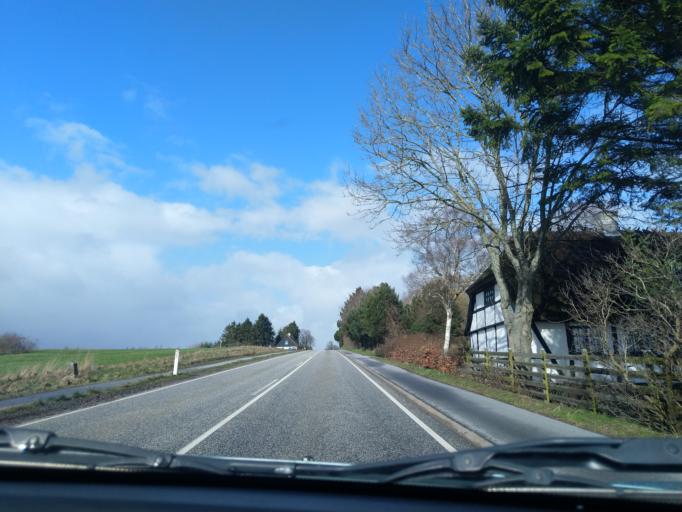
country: DK
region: Zealand
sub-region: Naestved Kommune
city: Naestved
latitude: 55.3043
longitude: 11.6894
